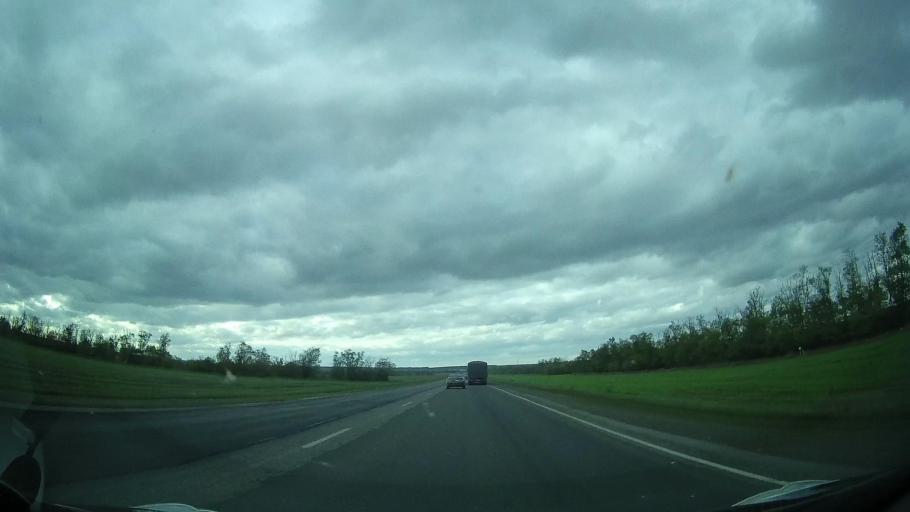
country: RU
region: Rostov
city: Kagal'nitskaya
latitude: 46.8633
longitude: 40.1810
